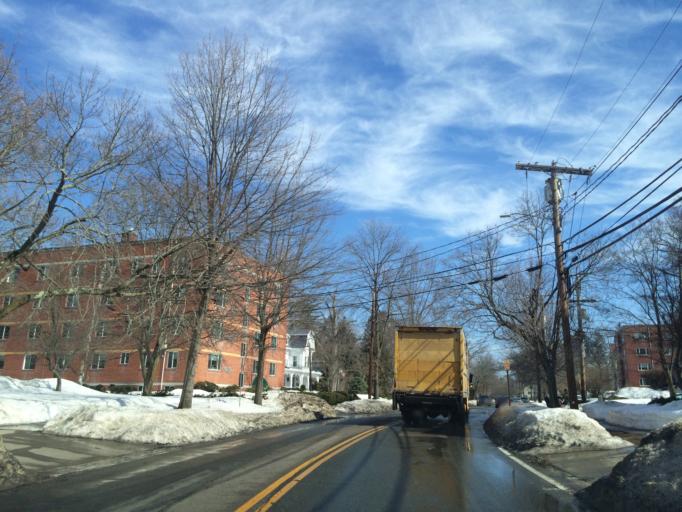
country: US
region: Massachusetts
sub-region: Middlesex County
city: Arlington
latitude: 42.4119
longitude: -71.1579
